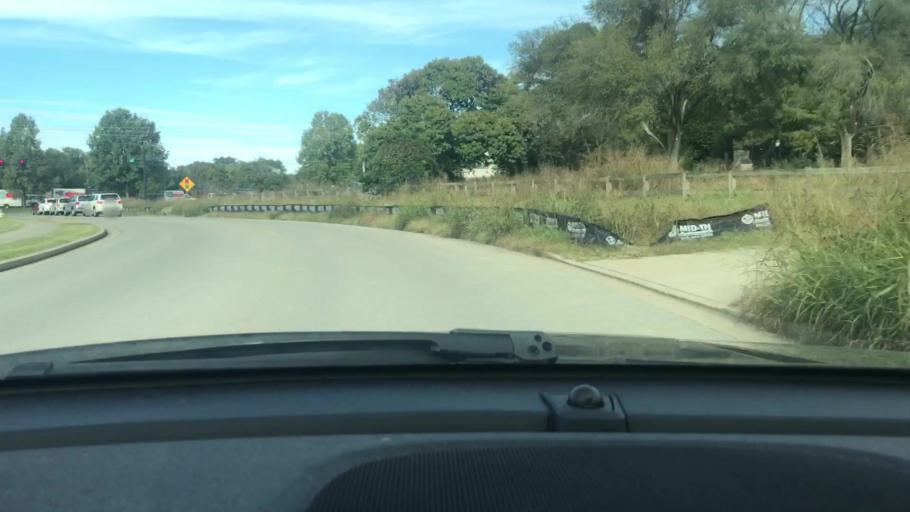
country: US
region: Tennessee
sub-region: Williamson County
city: Franklin
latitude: 35.9548
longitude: -86.8310
